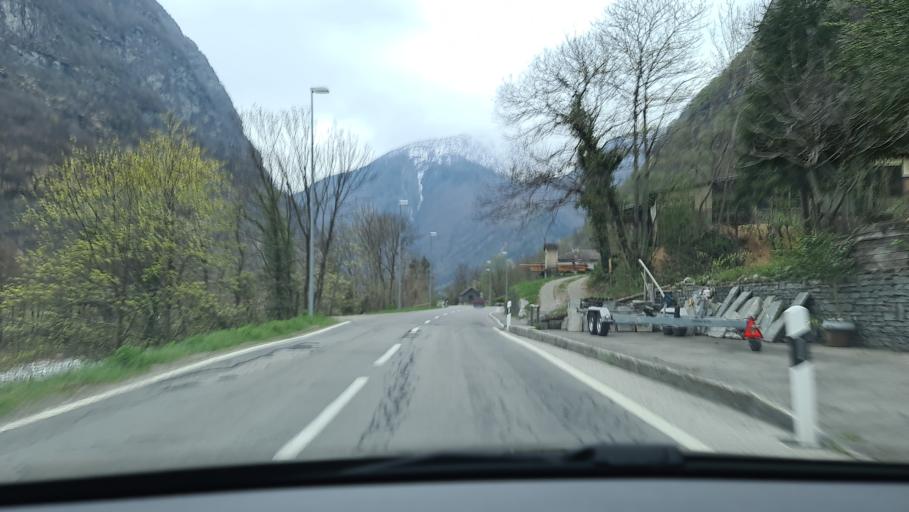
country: CH
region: Ticino
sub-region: Vallemaggia District
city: Cevio
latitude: 46.3375
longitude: 8.6067
